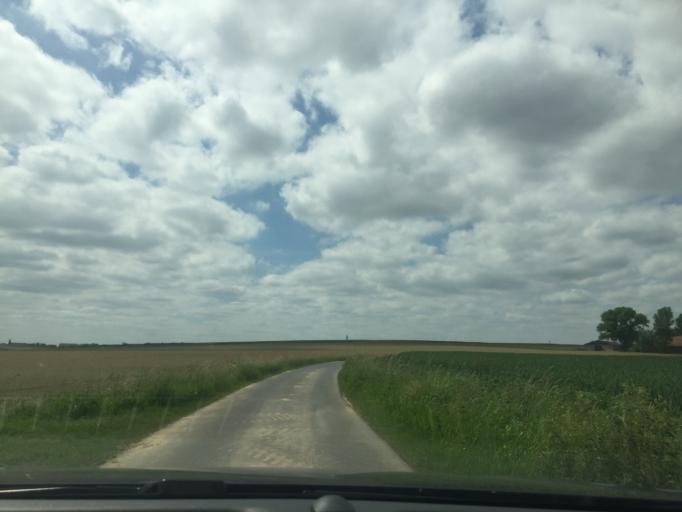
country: BE
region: Flanders
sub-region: Provincie West-Vlaanderen
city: Zwevegem
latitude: 50.7650
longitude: 3.3423
